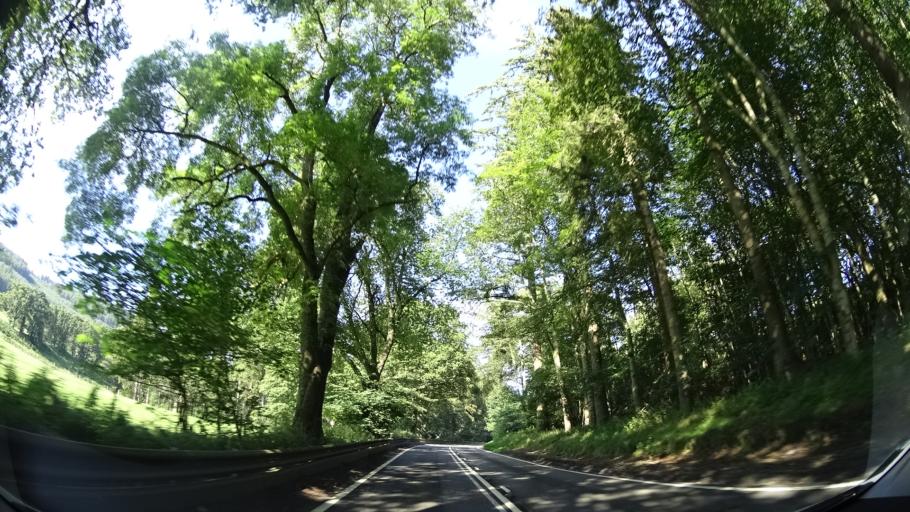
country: GB
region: Scotland
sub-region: Highland
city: Inverness
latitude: 57.4371
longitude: -4.3018
